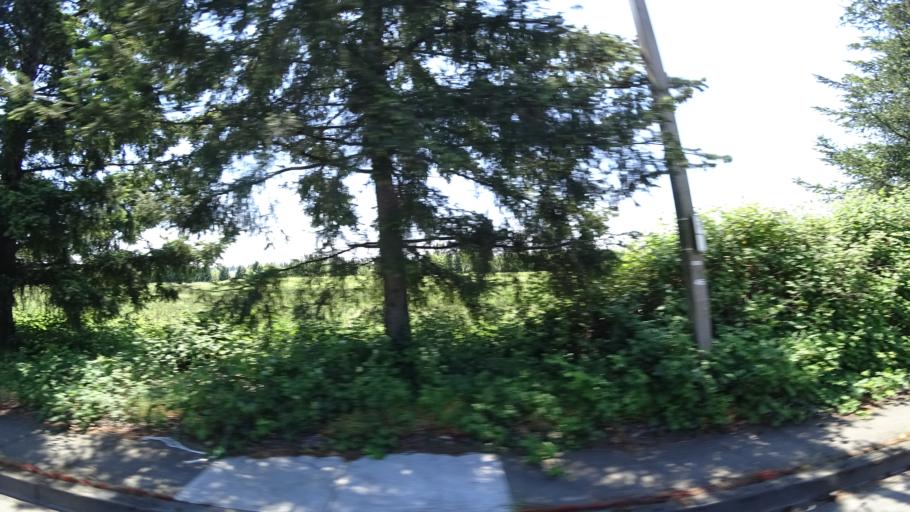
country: US
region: Oregon
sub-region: Multnomah County
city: Fairview
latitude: 45.5586
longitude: -122.5051
